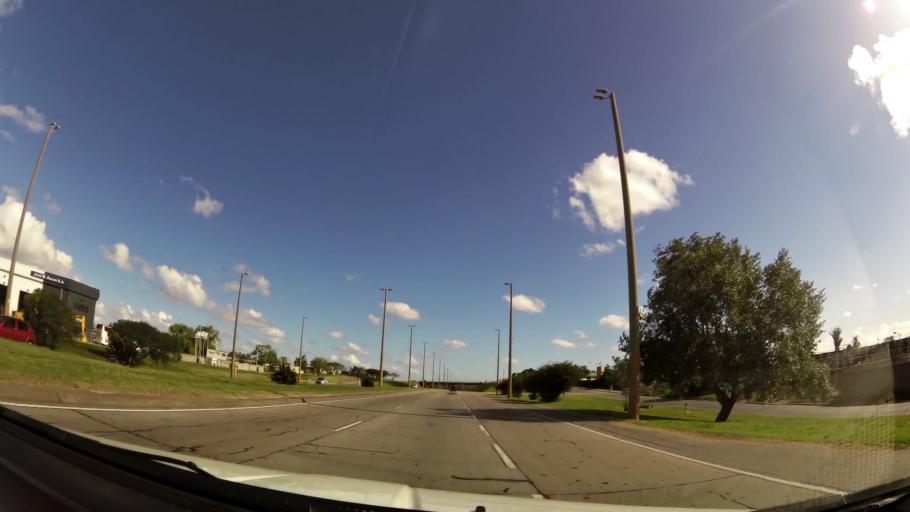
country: UY
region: Canelones
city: La Paz
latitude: -34.8409
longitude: -56.2541
